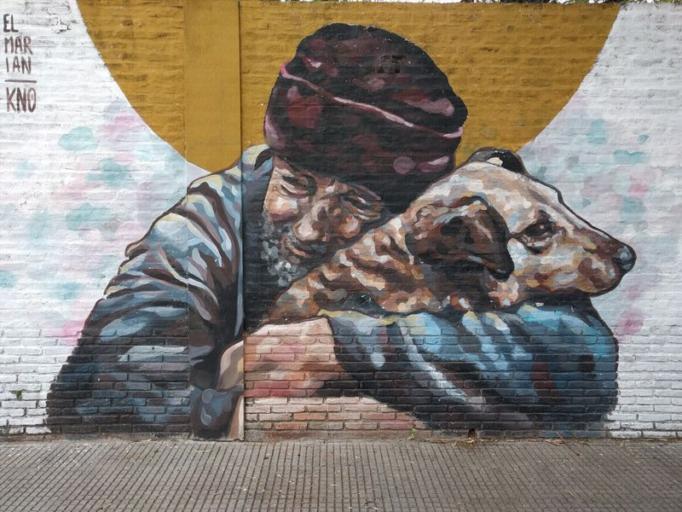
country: AR
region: Buenos Aires F.D.
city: Colegiales
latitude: -34.5591
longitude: -58.4794
